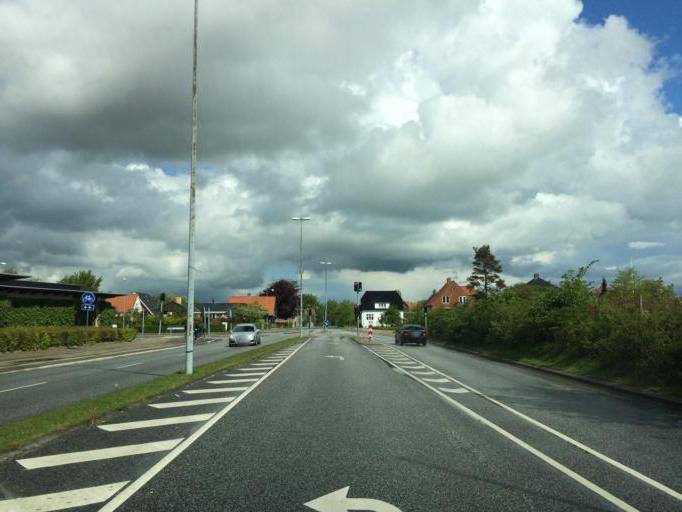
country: DK
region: Central Jutland
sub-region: Holstebro Kommune
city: Holstebro
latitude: 56.3645
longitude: 8.6115
